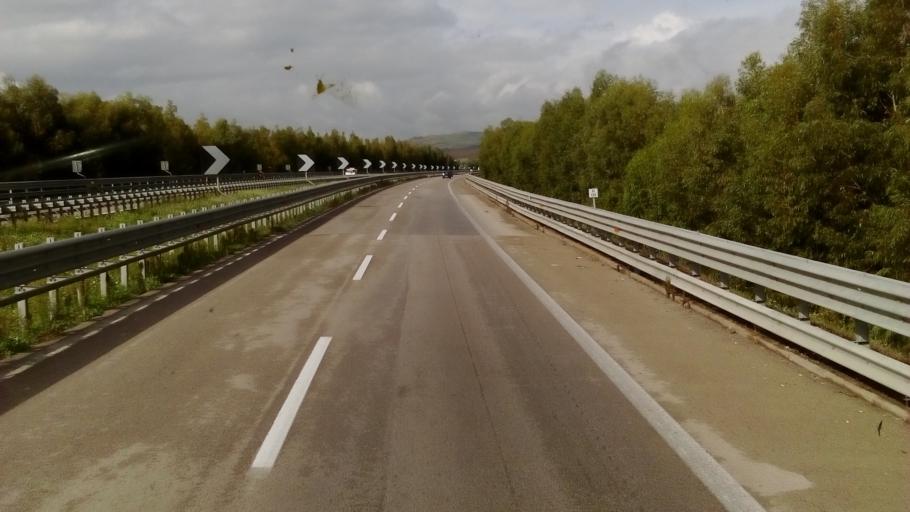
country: IT
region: Sicily
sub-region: Enna
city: Agira
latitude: 37.5634
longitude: 14.4986
